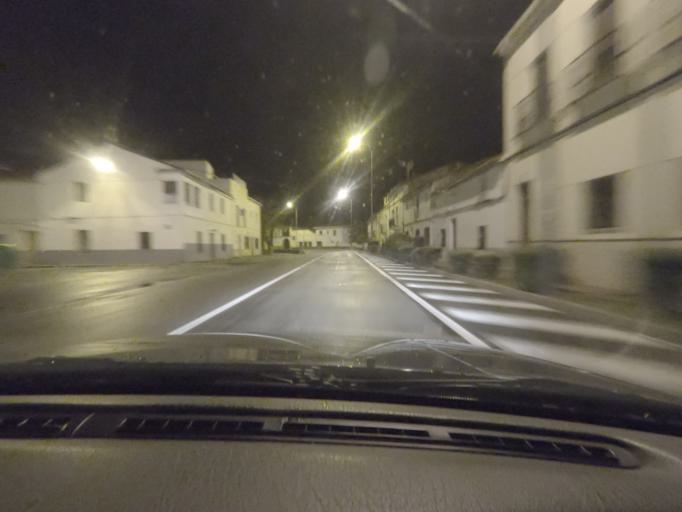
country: ES
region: Extremadura
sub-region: Provincia de Caceres
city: Canaveral
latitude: 39.7929
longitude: -6.3896
